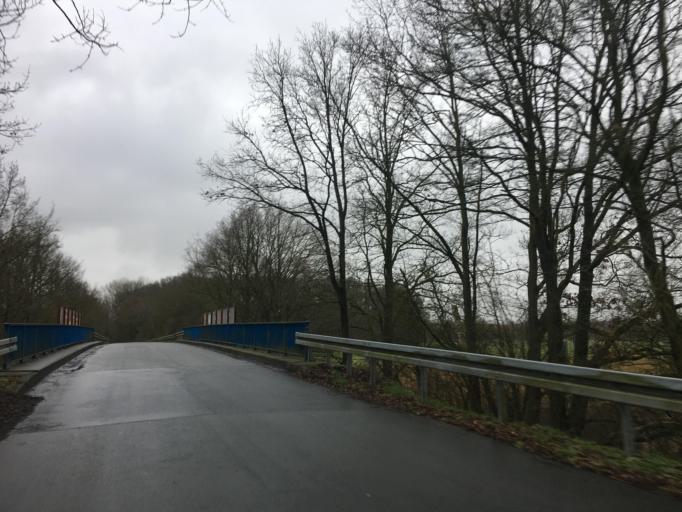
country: DE
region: North Rhine-Westphalia
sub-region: Regierungsbezirk Munster
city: Senden
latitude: 51.9168
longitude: 7.5386
